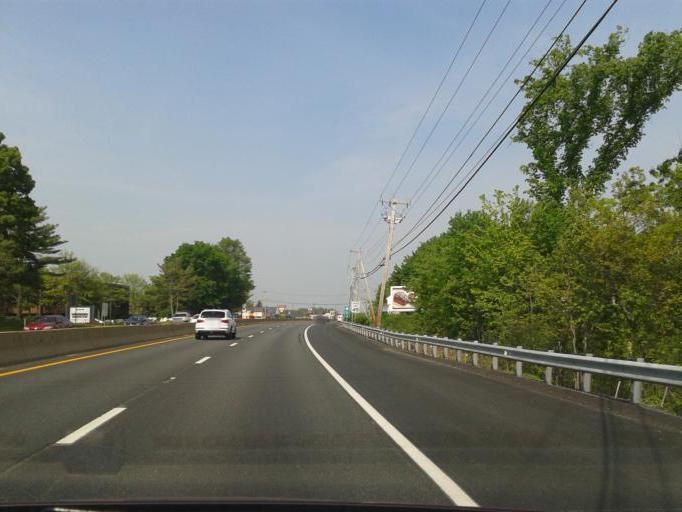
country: US
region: Massachusetts
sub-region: Worcester County
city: Westborough
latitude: 42.2851
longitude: -71.6021
